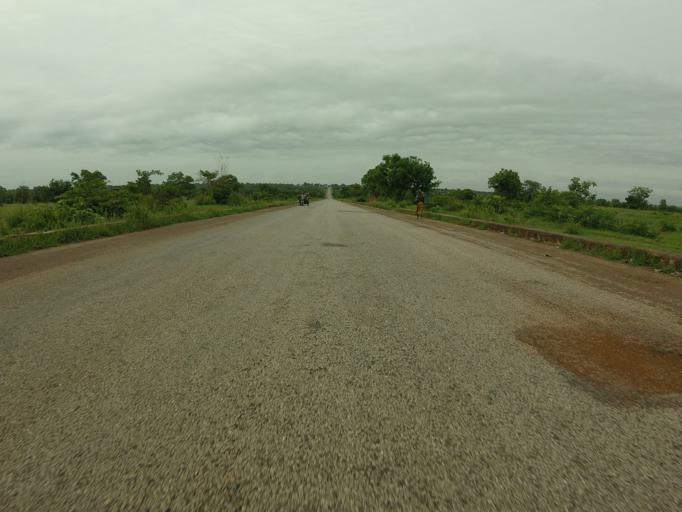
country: GH
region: Northern
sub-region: Yendi
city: Yendi
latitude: 9.4979
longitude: -0.0236
